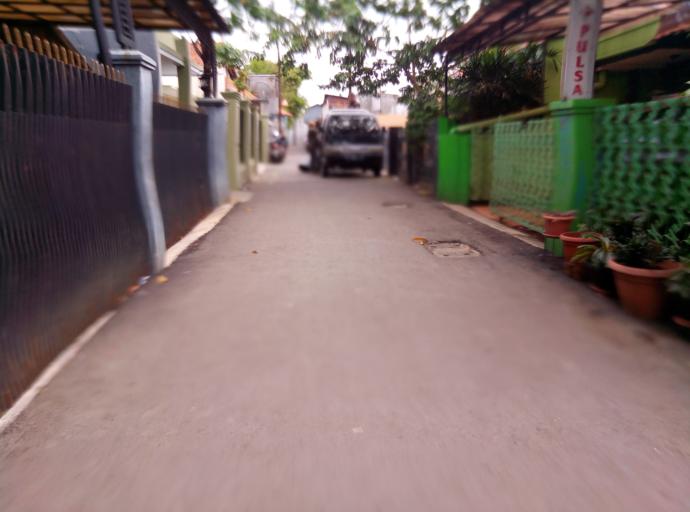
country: ID
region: West Java
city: Bandung
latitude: -6.9368
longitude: 107.6436
